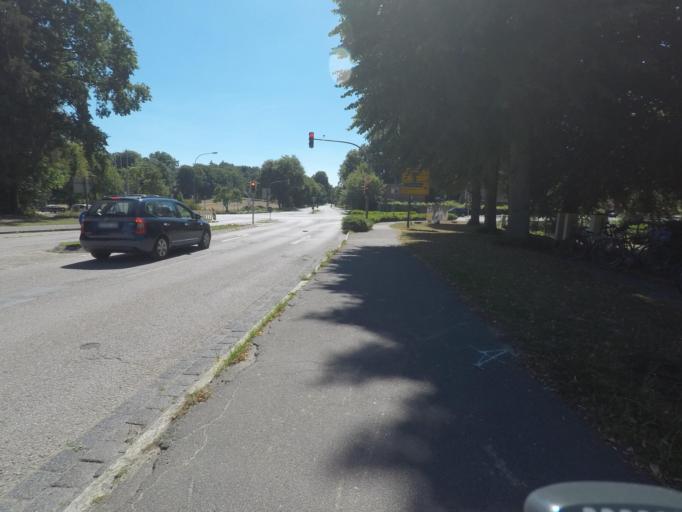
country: DE
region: Schleswig-Holstein
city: Lutjensee
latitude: 53.6453
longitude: 10.3611
